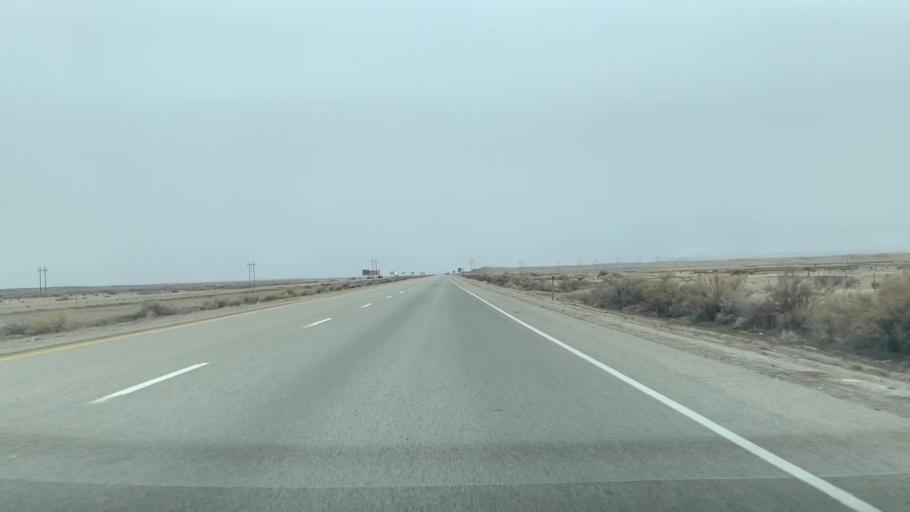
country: US
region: Utah
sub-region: Carbon County
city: East Carbon City
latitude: 38.9889
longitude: -110.1994
